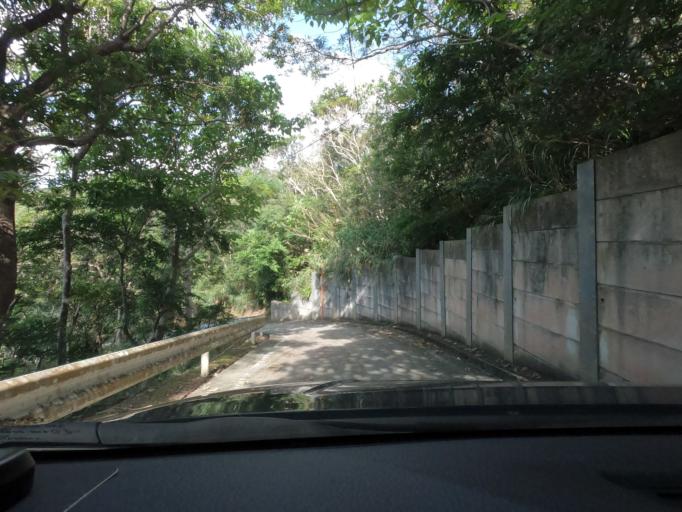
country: JP
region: Okinawa
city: Nago
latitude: 26.7566
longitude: 128.1988
